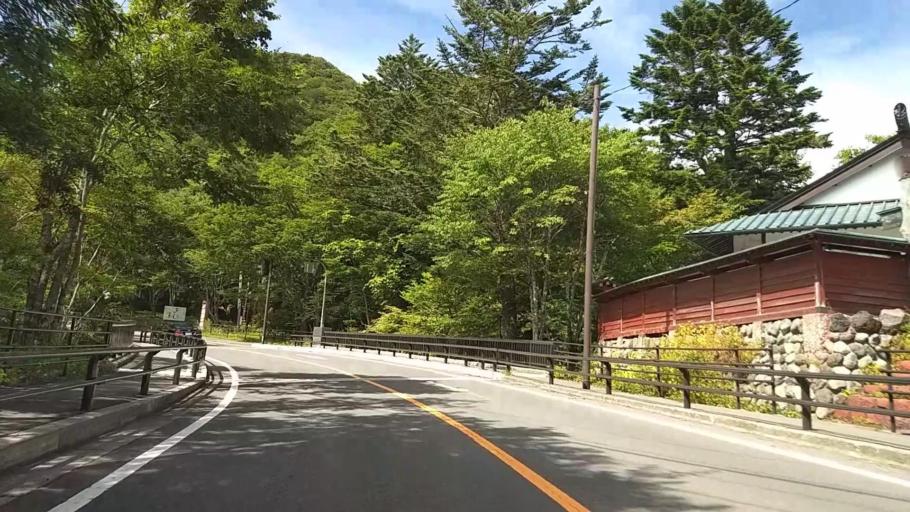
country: JP
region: Tochigi
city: Nikko
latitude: 36.7570
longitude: 139.4515
